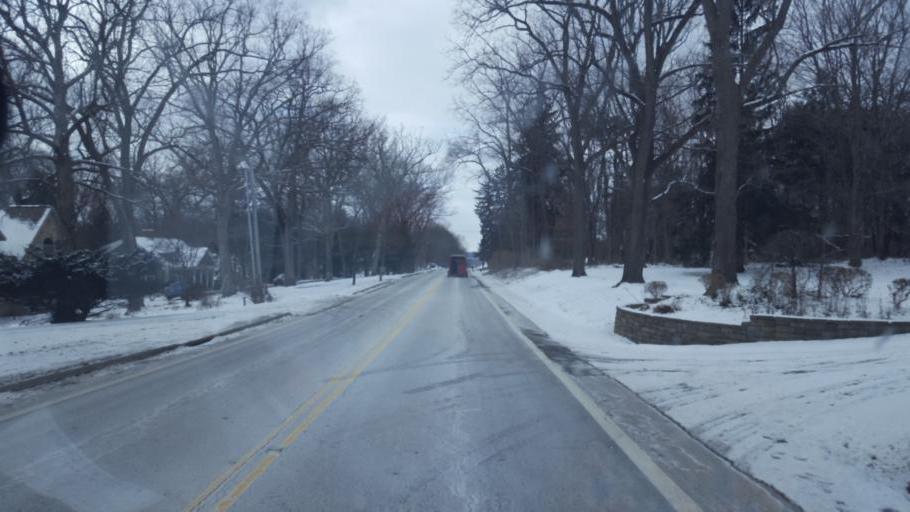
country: US
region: Ohio
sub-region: Knox County
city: Mount Vernon
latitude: 40.3888
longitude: -82.4548
